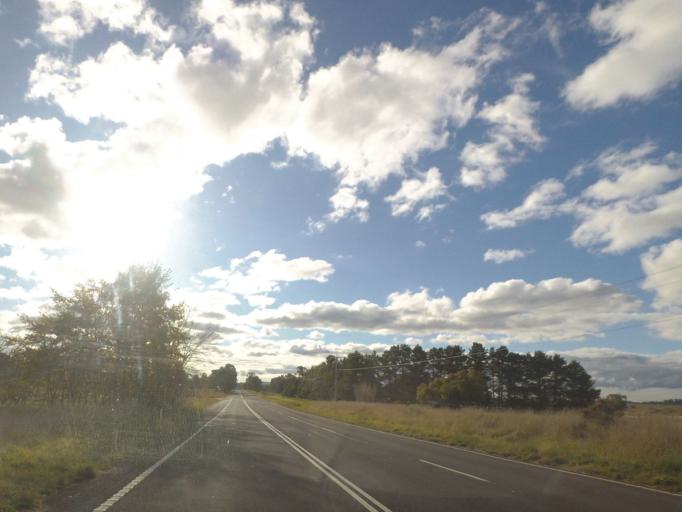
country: AU
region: Victoria
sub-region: Mount Alexander
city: Castlemaine
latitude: -37.1568
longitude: 144.3550
